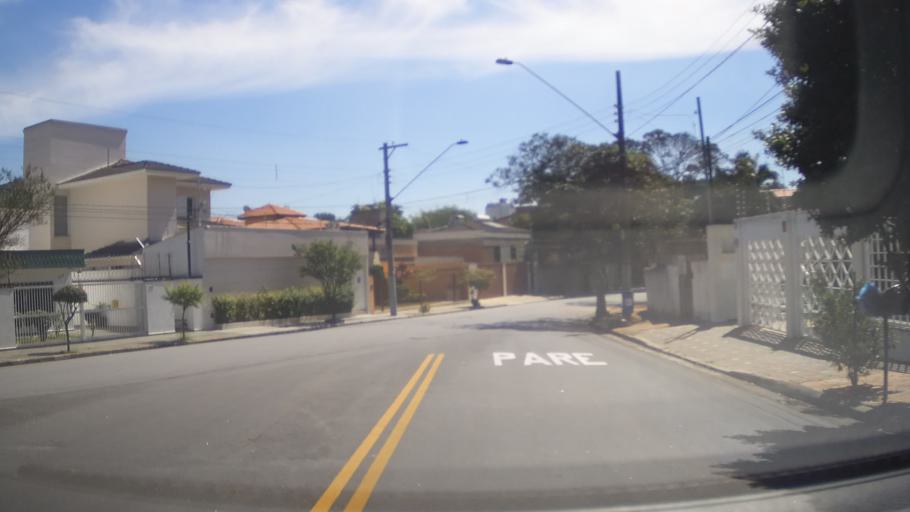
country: BR
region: Sao Paulo
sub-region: Sao Caetano Do Sul
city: Sao Caetano do Sul
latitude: -23.6398
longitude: -46.5795
